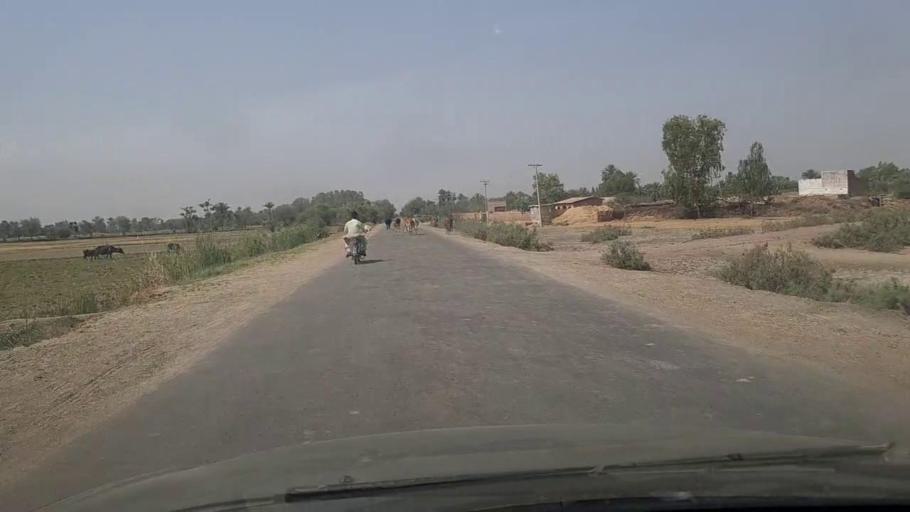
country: PK
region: Sindh
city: Khanpur
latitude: 27.8946
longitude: 69.4880
